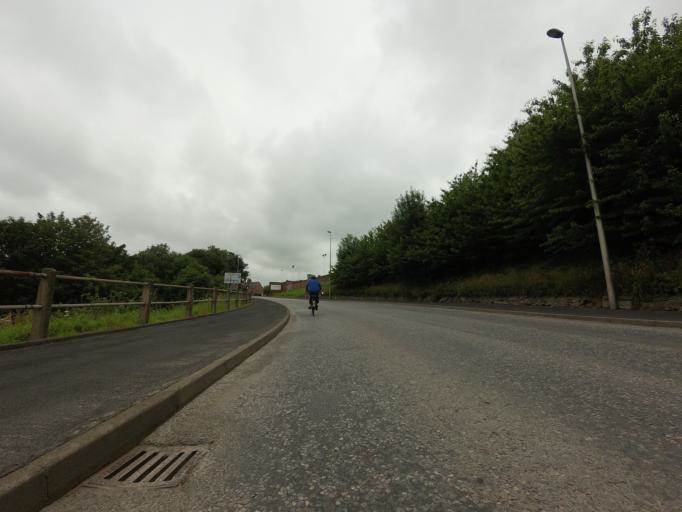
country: GB
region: Scotland
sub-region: Aberdeenshire
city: Turriff
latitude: 57.5364
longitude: -2.4633
